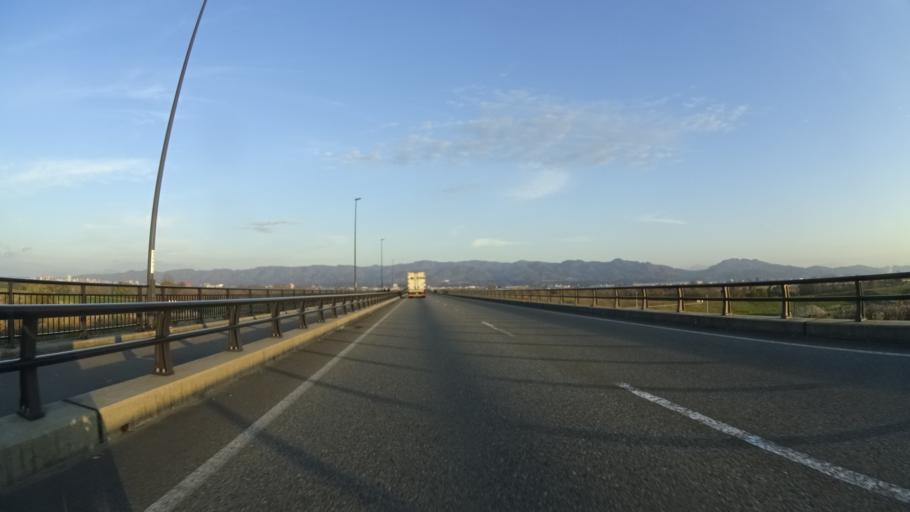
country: JP
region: Niigata
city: Nagaoka
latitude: 37.4326
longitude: 138.8152
